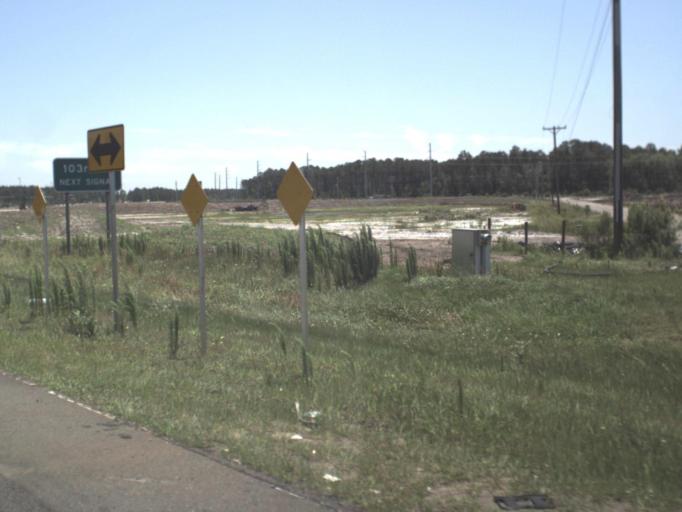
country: US
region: Florida
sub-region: Clay County
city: Bellair-Meadowbrook Terrace
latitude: 30.2511
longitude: -81.8485
